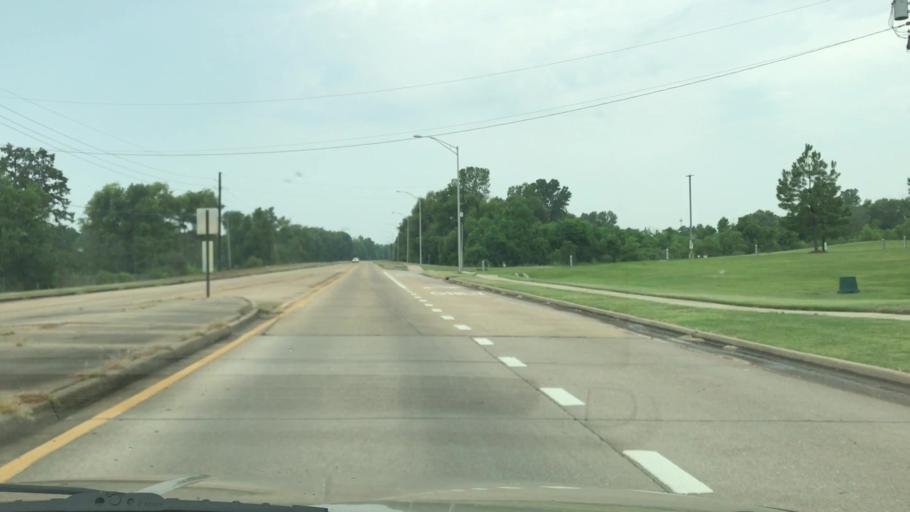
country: US
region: Louisiana
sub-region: Bossier Parish
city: Bossier City
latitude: 32.4756
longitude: -93.6945
